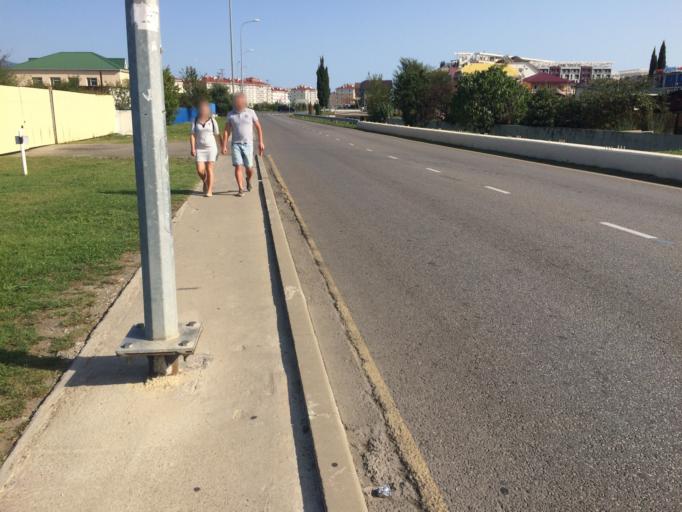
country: RU
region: Krasnodarskiy
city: Adler
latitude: 43.3938
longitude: 39.9861
